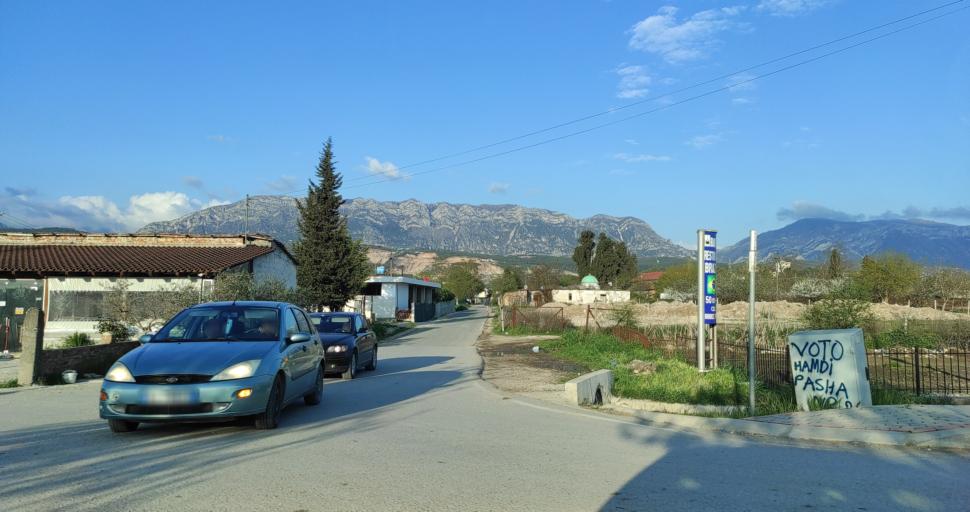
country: AL
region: Durres
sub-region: Rrethi i Krujes
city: Fushe-Kruje
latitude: 41.4871
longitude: 19.7262
